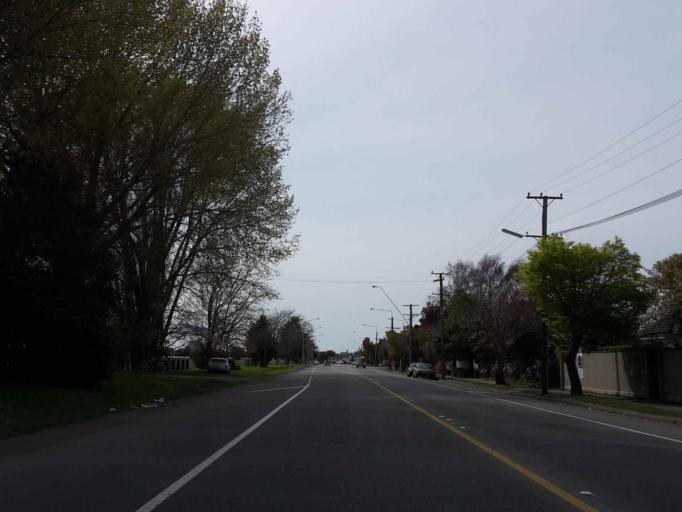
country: NZ
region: Canterbury
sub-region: Waimakariri District
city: Kaiapoi
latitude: -43.4516
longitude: 172.6220
